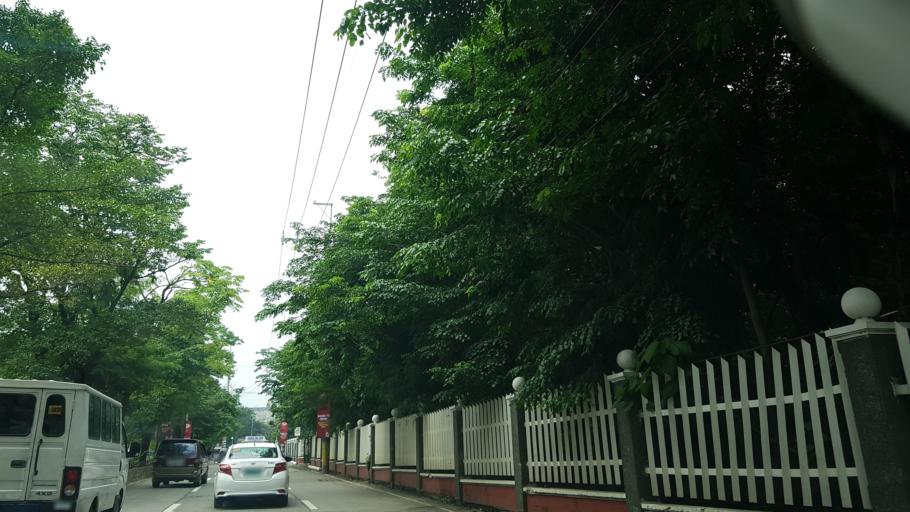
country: PH
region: Metro Manila
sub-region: Makati City
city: Makati City
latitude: 14.5332
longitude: 121.0410
